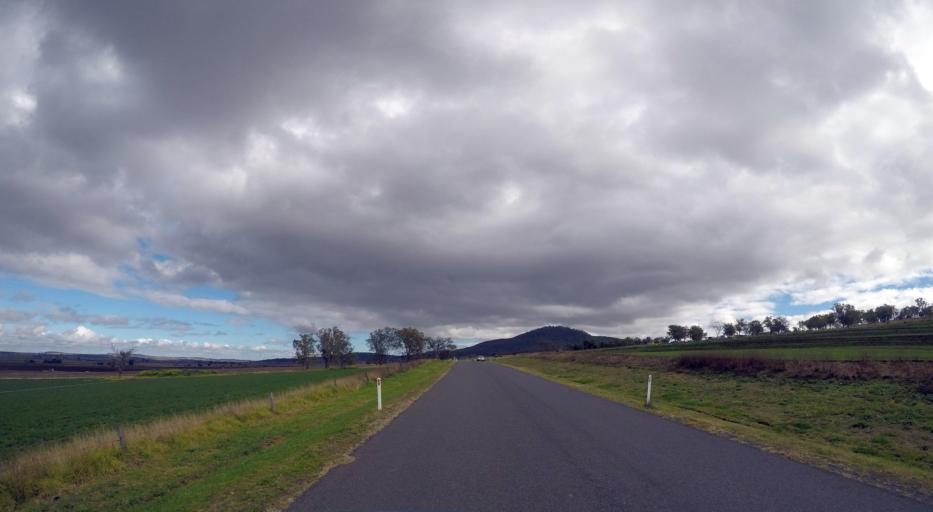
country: AU
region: Queensland
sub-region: Southern Downs
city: Warwick
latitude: -28.0674
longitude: 152.1466
